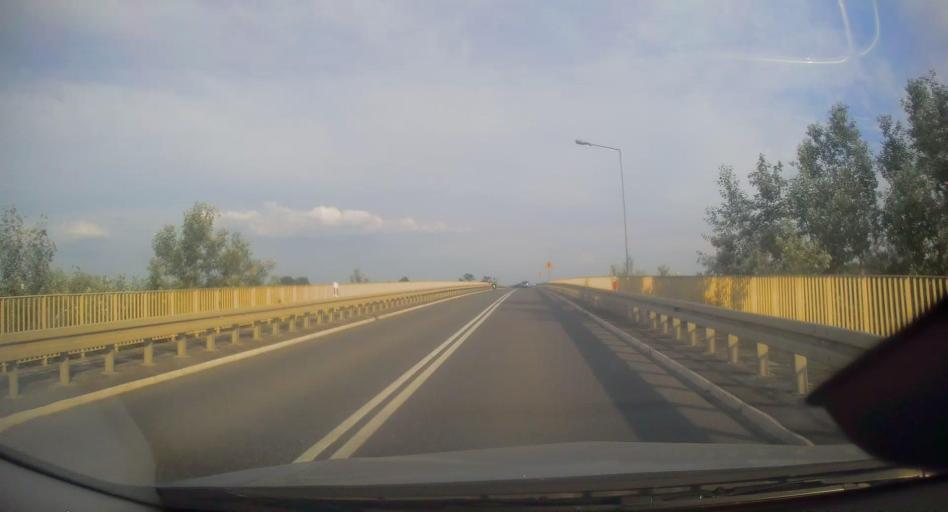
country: PL
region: Lesser Poland Voivodeship
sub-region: Powiat brzeski
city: Szczurowa
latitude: 50.1544
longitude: 20.6085
